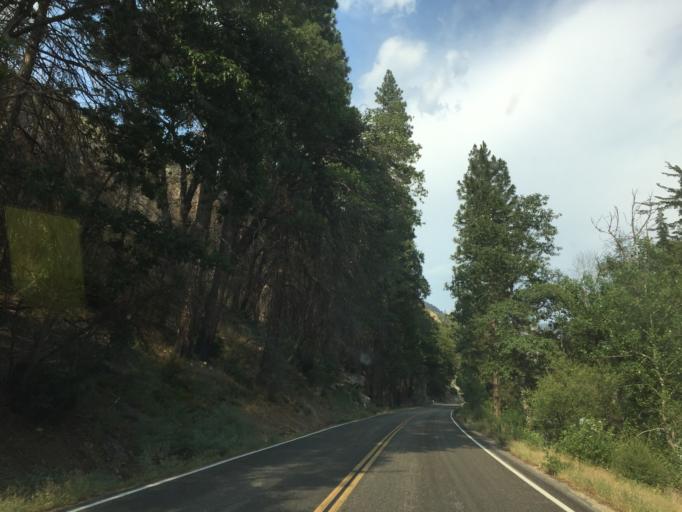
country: US
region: California
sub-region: Tulare County
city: Three Rivers
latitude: 36.8031
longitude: -118.7300
